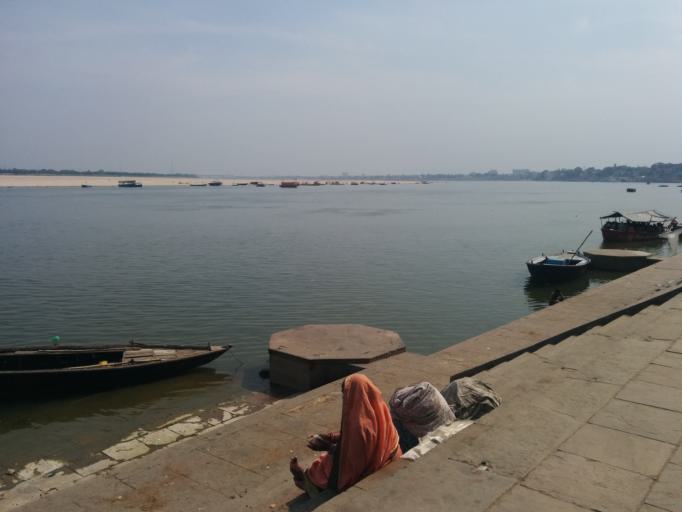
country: IN
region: Uttar Pradesh
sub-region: Varanasi
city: Varanasi
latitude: 25.3096
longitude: 83.0129
